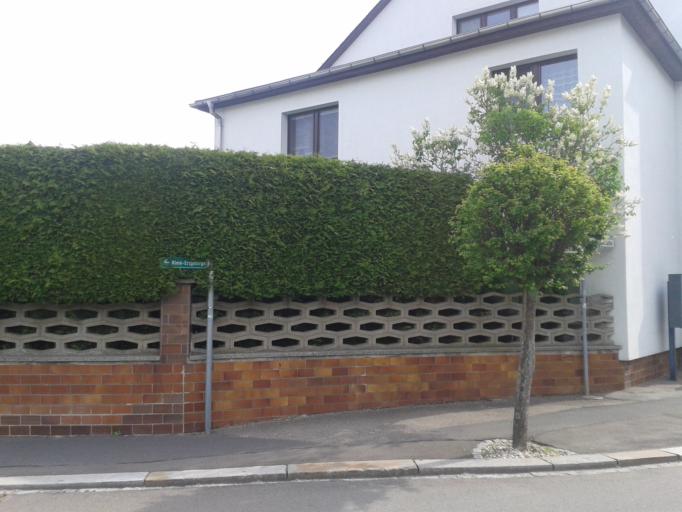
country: DE
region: Saxony
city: Oederan
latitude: 50.8578
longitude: 13.1770
